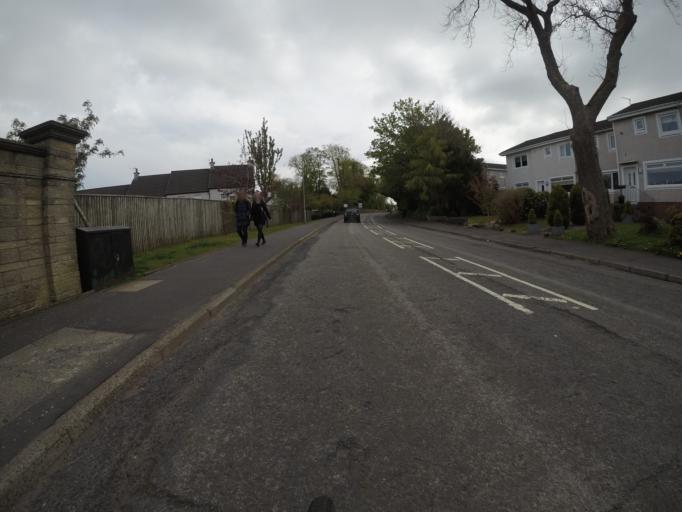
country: GB
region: Scotland
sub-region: East Renfrewshire
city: Busby
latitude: 55.7756
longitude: -4.3050
